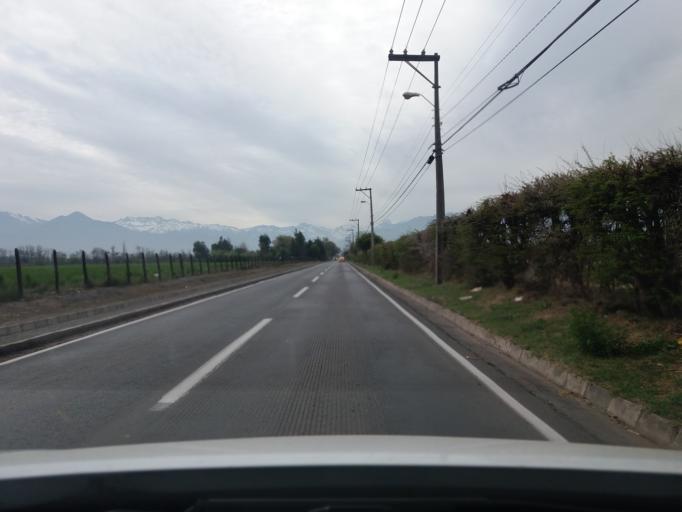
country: CL
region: Valparaiso
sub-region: Provincia de Los Andes
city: Los Andes
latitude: -32.8197
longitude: -70.6795
